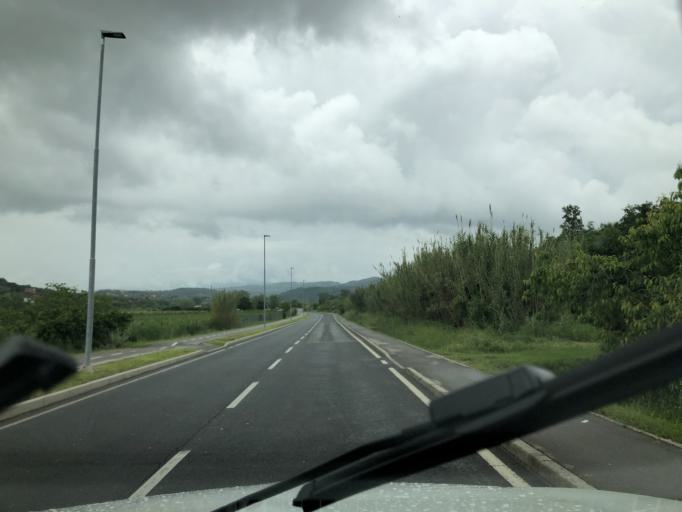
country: SI
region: Koper-Capodistria
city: Prade
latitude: 45.5194
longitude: 13.7496
